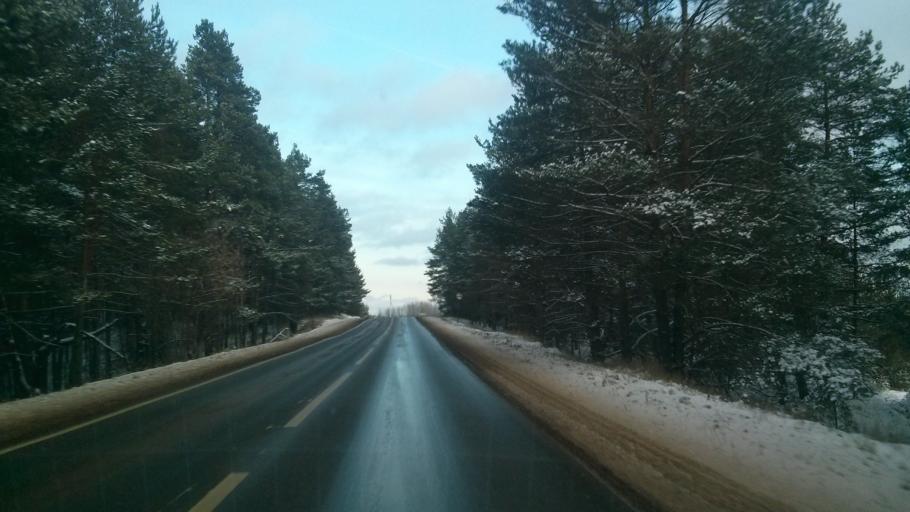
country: RU
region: Nizjnij Novgorod
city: Navashino
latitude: 55.6029
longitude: 42.1719
